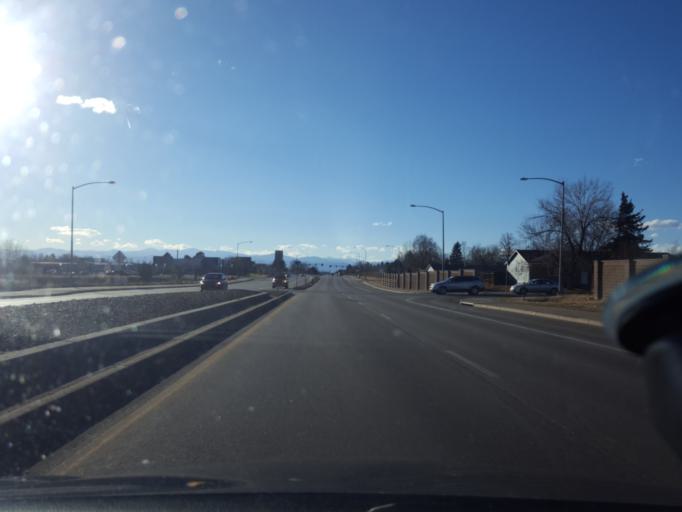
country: US
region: Colorado
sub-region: Adams County
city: Aurora
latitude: 39.7256
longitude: -104.7956
